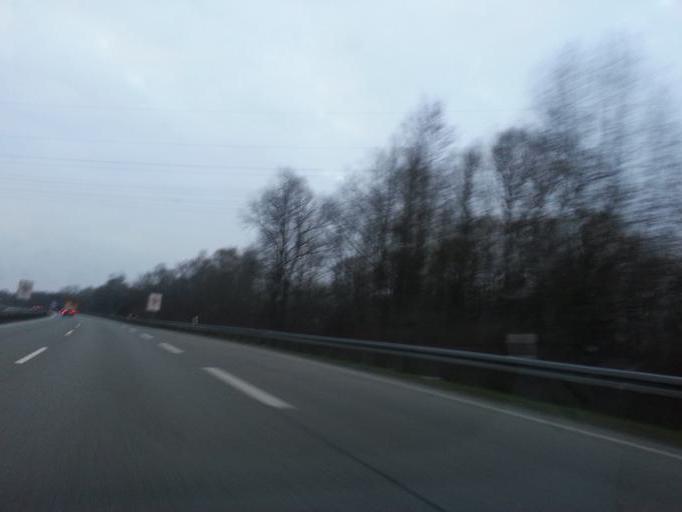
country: DE
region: Baden-Wuerttemberg
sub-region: Tuebingen Region
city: Berg
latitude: 47.8003
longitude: 9.6079
